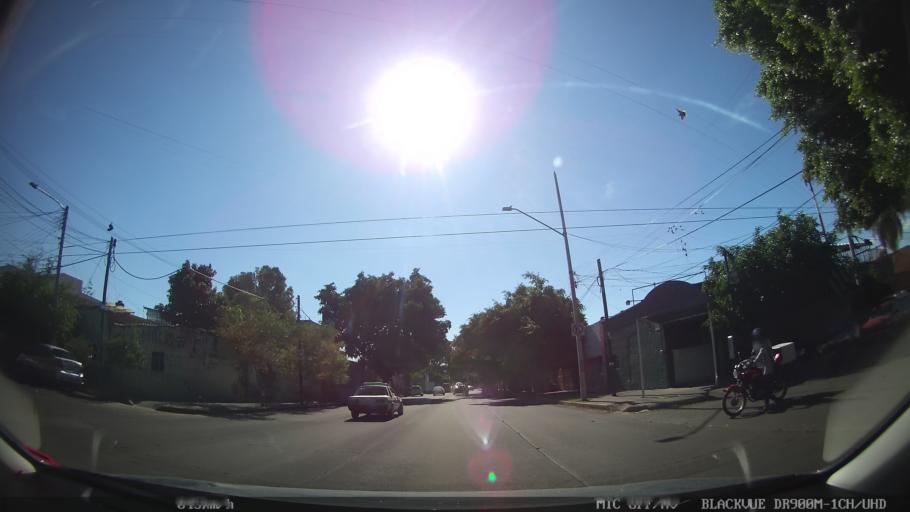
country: MX
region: Jalisco
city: Tlaquepaque
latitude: 20.6658
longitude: -103.3075
